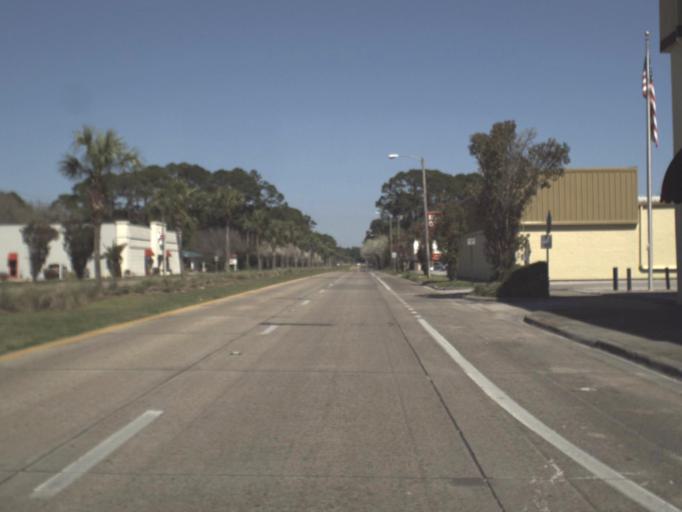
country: US
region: Florida
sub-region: Gulf County
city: Port Saint Joe
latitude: 29.8125
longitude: -85.3007
